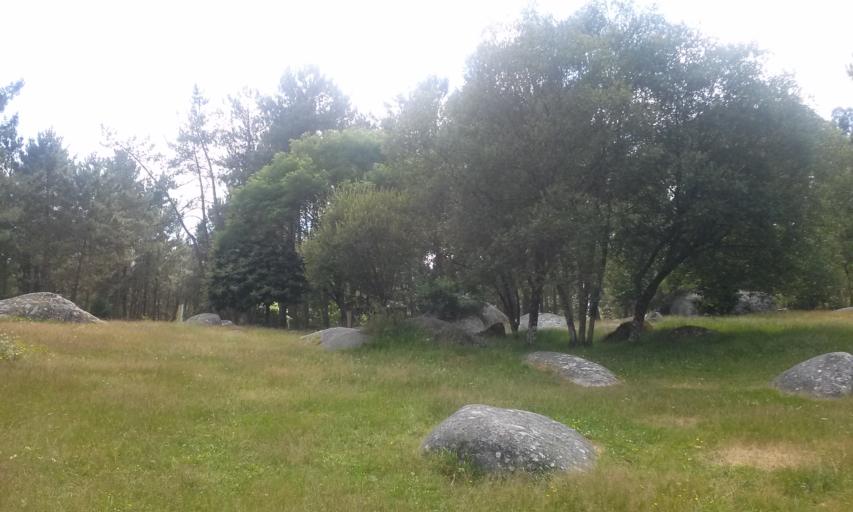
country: ES
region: Galicia
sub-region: Provincia de Lugo
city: Begonte
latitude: 43.1200
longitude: -7.6797
